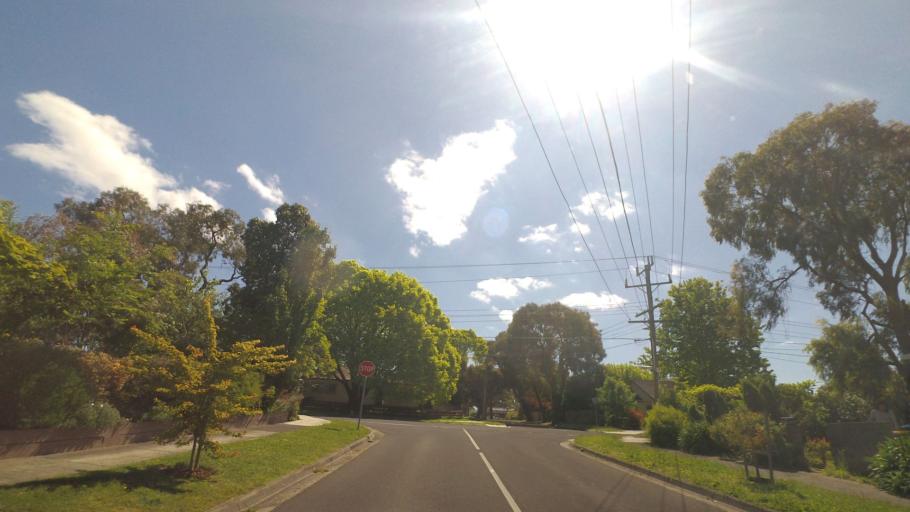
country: AU
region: Victoria
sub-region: Knox
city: Bayswater
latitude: -37.8555
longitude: 145.2757
